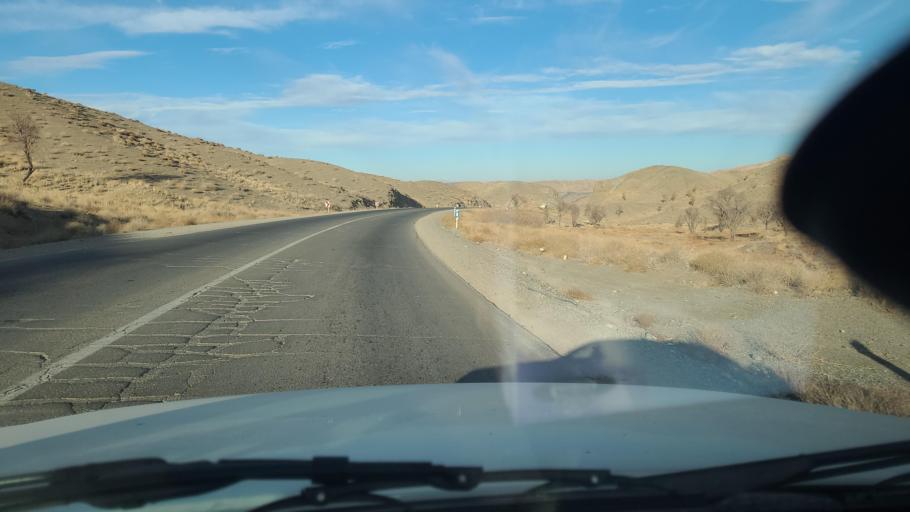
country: IR
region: Razavi Khorasan
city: Sabzevar
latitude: 36.4151
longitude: 57.5518
